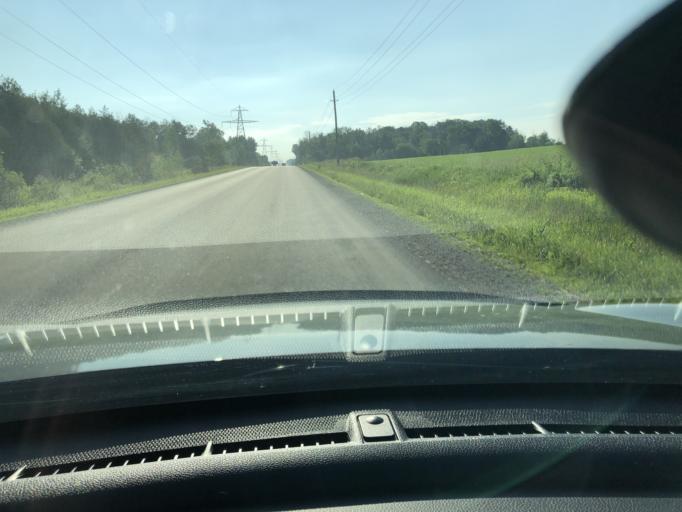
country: CA
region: Ontario
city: Stratford
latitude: 43.3883
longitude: -80.8717
